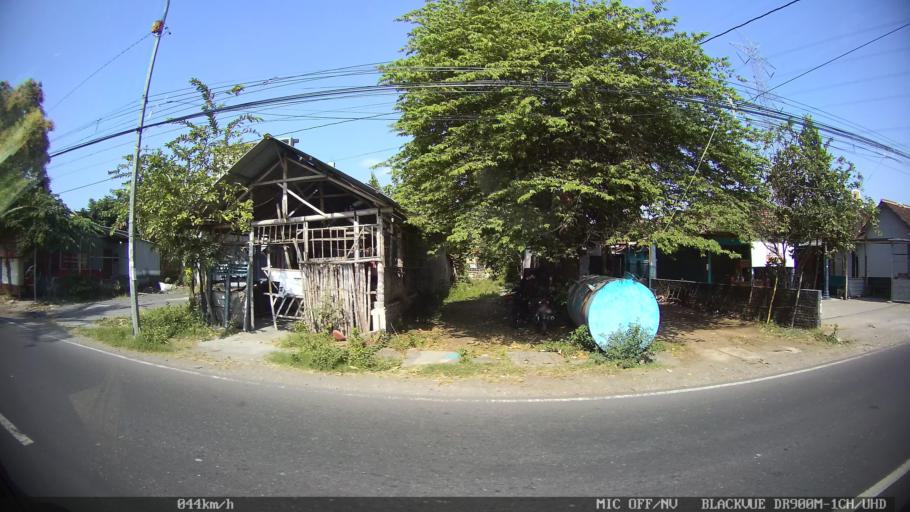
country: ID
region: Daerah Istimewa Yogyakarta
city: Sewon
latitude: -7.8833
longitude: 110.3889
